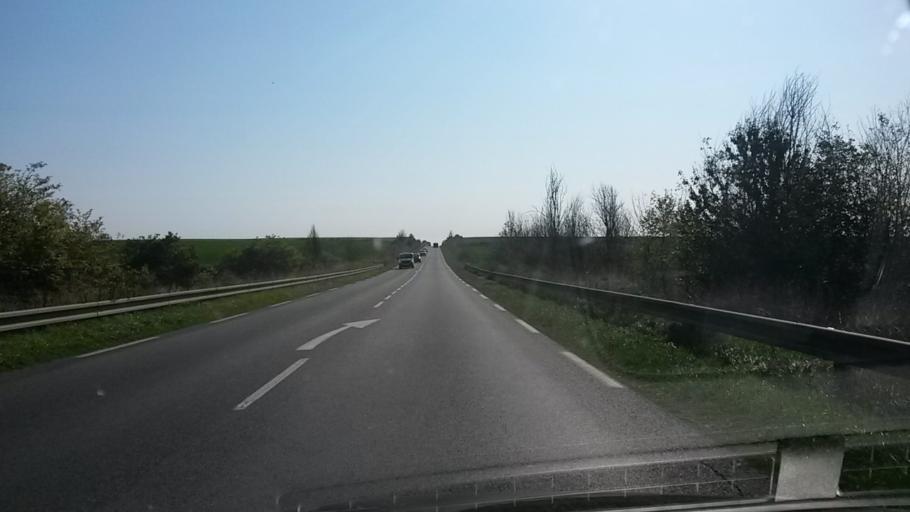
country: FR
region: Picardie
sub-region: Departement de l'Aisne
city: Homblieres
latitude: 49.8428
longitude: 3.4212
